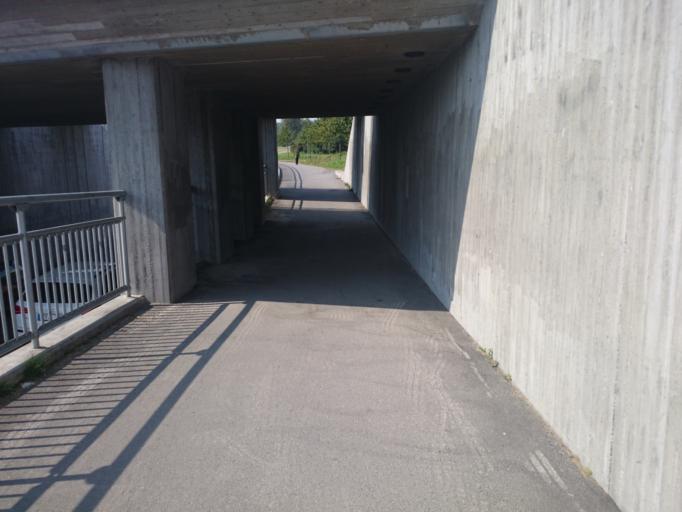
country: SE
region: Vaesternorrland
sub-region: Haernoesands Kommun
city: Haernoesand
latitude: 62.6374
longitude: 17.9313
